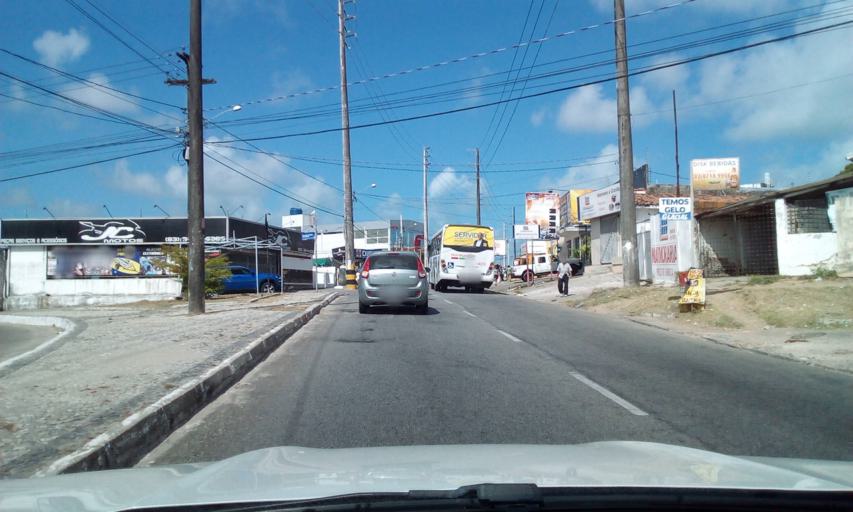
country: BR
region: Paraiba
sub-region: Joao Pessoa
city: Joao Pessoa
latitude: -7.1036
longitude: -34.8641
